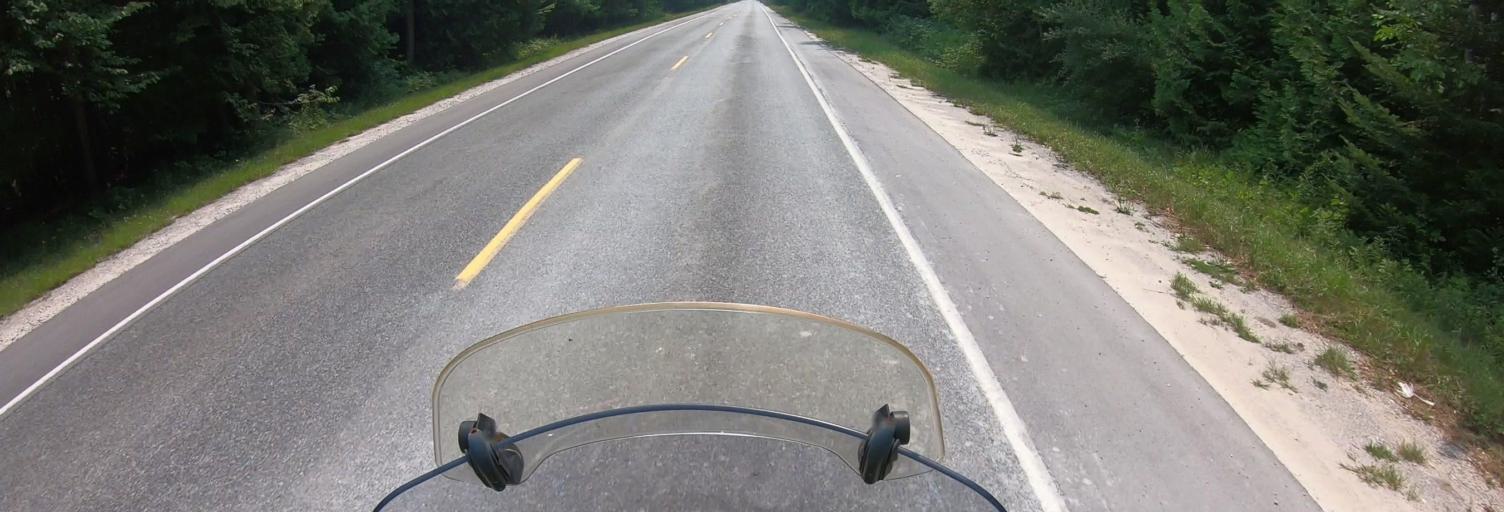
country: US
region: Michigan
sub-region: Leelanau County
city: Leland
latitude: 45.2043
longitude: -85.5455
